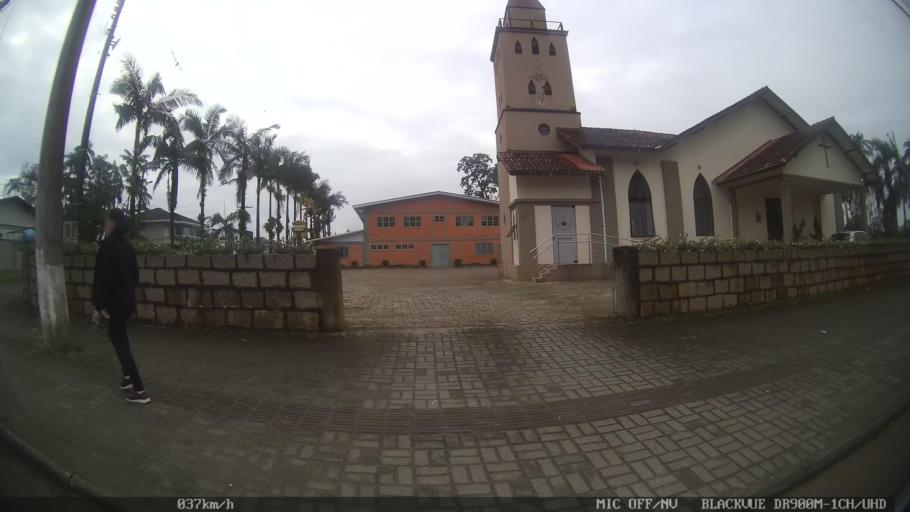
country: BR
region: Santa Catarina
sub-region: Joinville
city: Joinville
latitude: -26.0434
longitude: -48.8557
